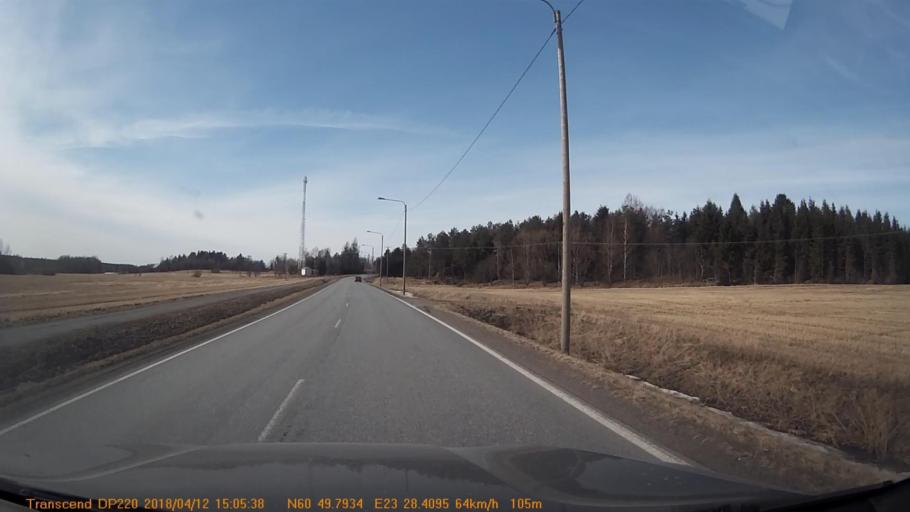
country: FI
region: Haeme
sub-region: Forssa
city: Jokioinen
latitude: 60.8301
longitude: 23.4731
